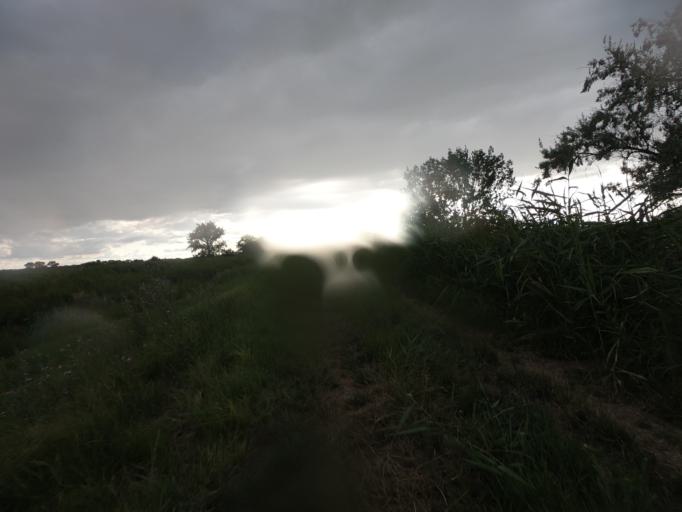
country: HU
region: Heves
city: Poroszlo
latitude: 47.7017
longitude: 20.6158
